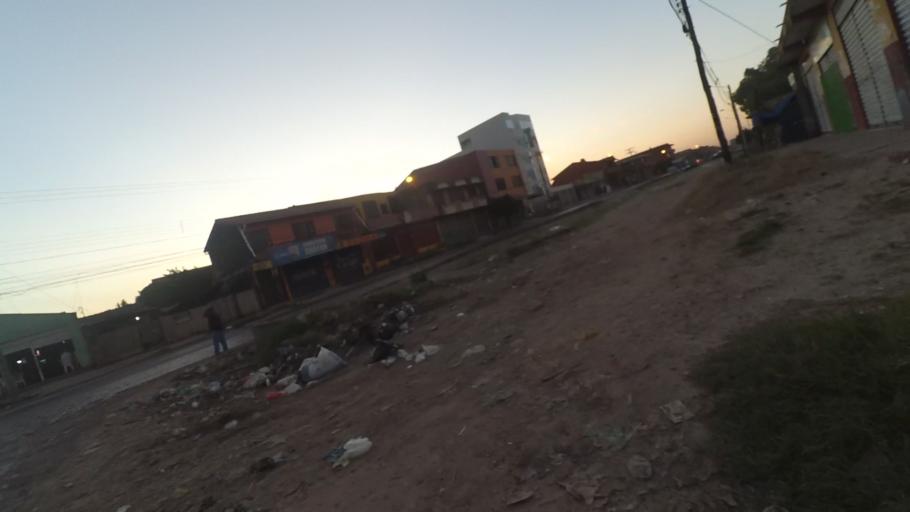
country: BO
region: Santa Cruz
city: Santa Cruz de la Sierra
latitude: -17.8219
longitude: -63.1350
